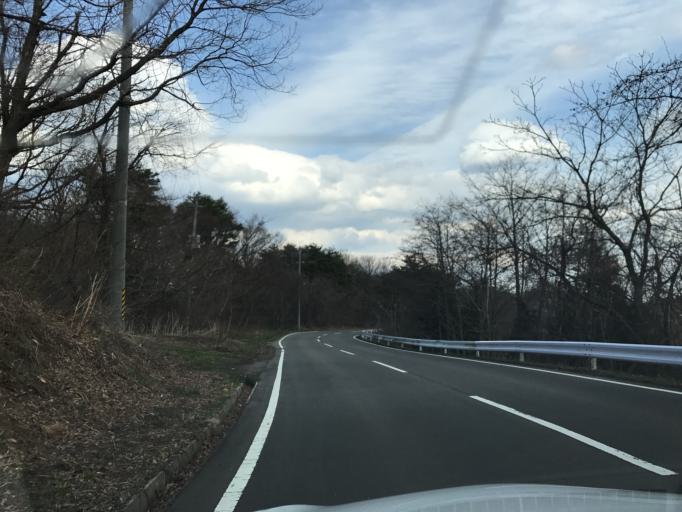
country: JP
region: Miyagi
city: Shiroishi
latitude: 38.0323
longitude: 140.5375
